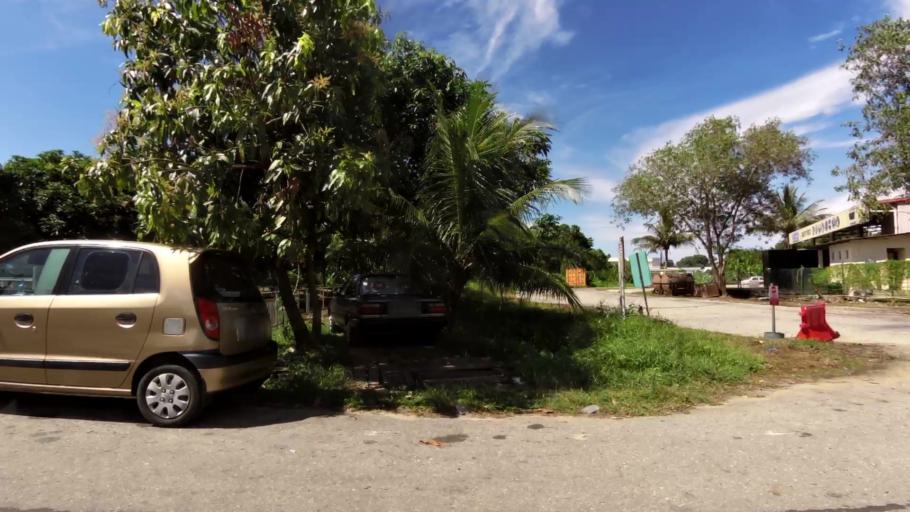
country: BN
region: Brunei and Muara
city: Bandar Seri Begawan
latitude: 4.9769
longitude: 114.9515
